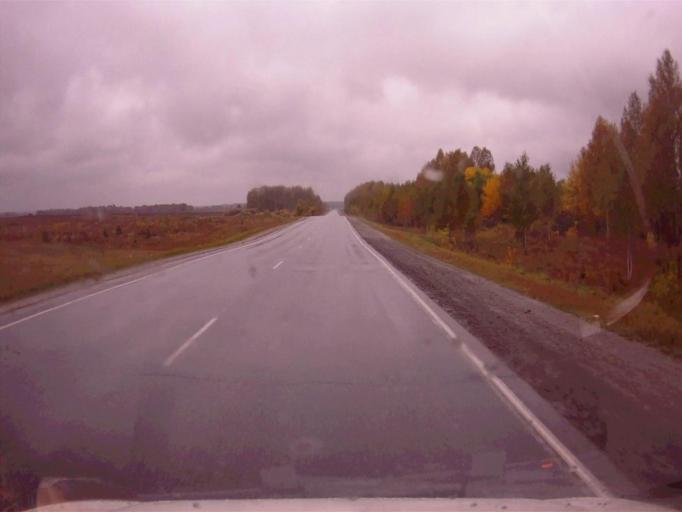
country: RU
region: Chelyabinsk
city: Argayash
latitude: 55.4785
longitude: 60.8336
